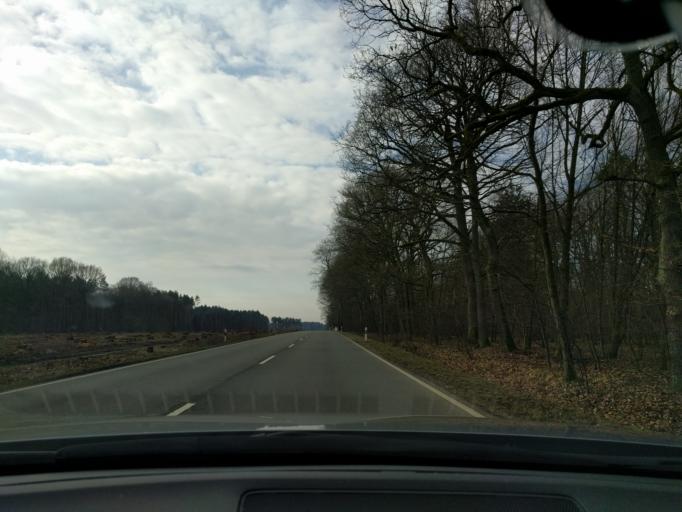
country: DE
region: Saxony-Anhalt
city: Colbitz
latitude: 52.3574
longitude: 11.6102
